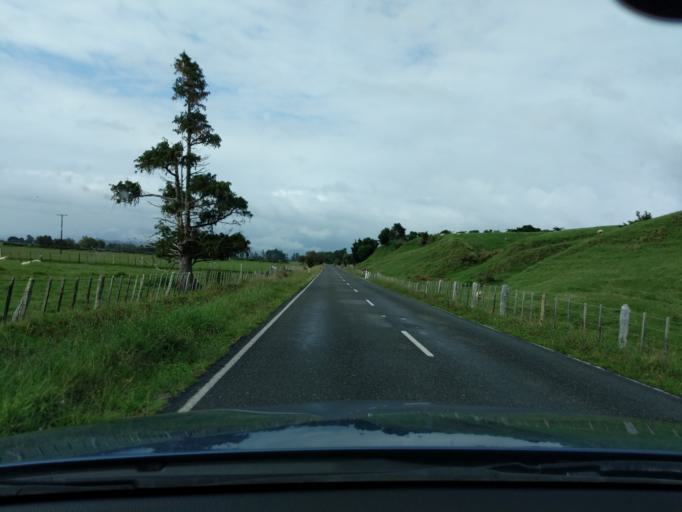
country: NZ
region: Tasman
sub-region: Tasman District
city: Takaka
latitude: -40.6291
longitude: 172.6734
